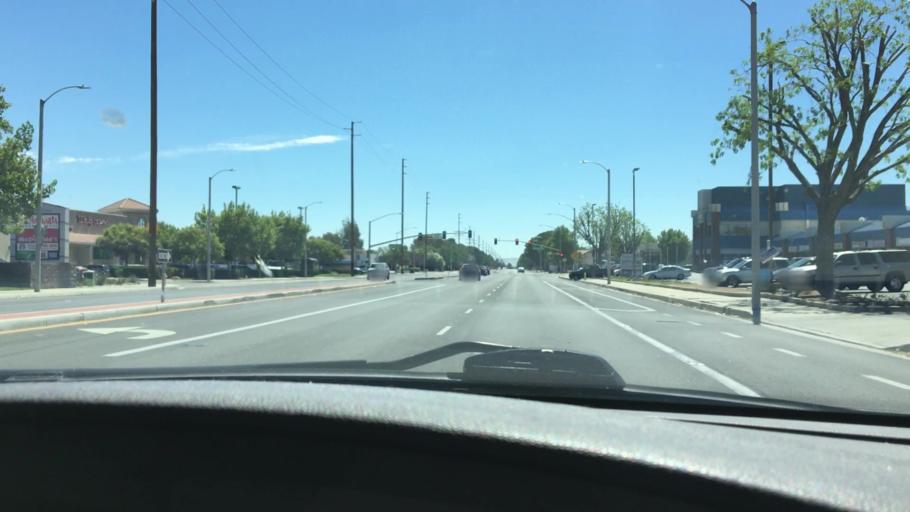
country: US
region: California
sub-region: Los Angeles County
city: Lancaster
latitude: 34.6749
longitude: -118.1142
